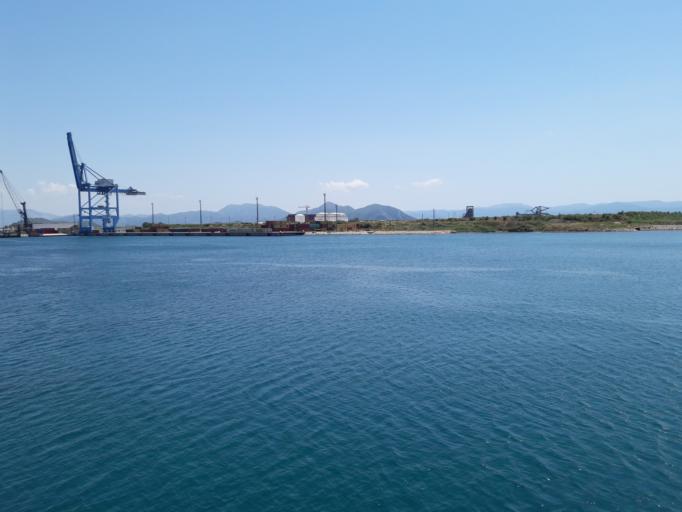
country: HR
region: Dubrovacko-Neretvanska
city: Komin
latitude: 43.0464
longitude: 17.4222
